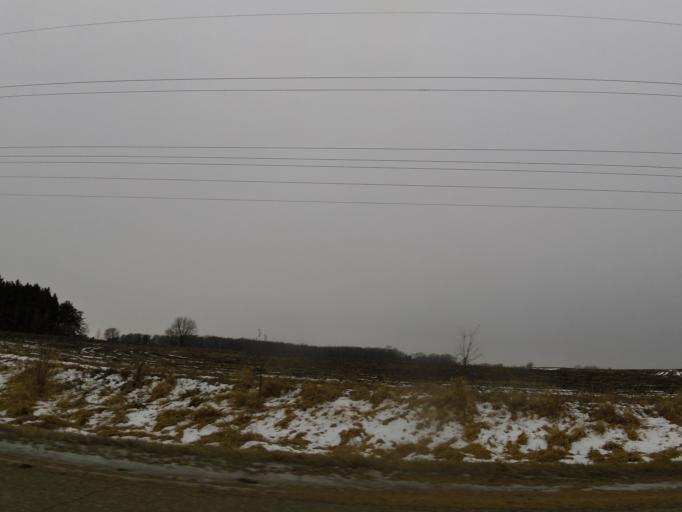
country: US
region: Minnesota
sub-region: Scott County
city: Jordan
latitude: 44.6446
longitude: -93.6248
